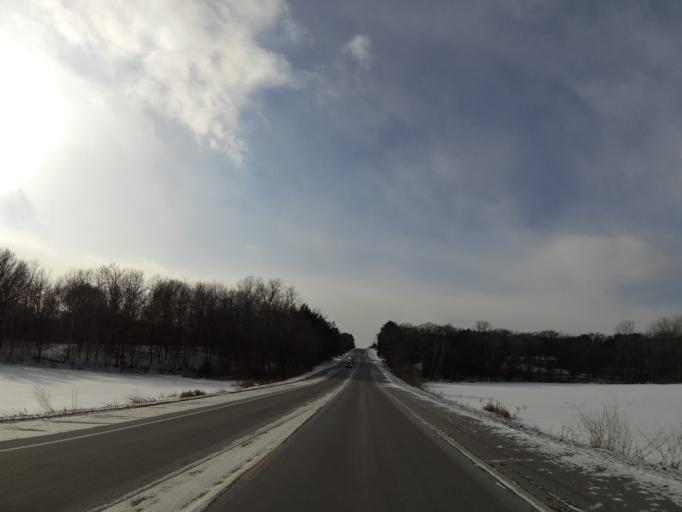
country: US
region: Minnesota
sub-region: Washington County
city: Lake Elmo
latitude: 44.9637
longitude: -92.9104
